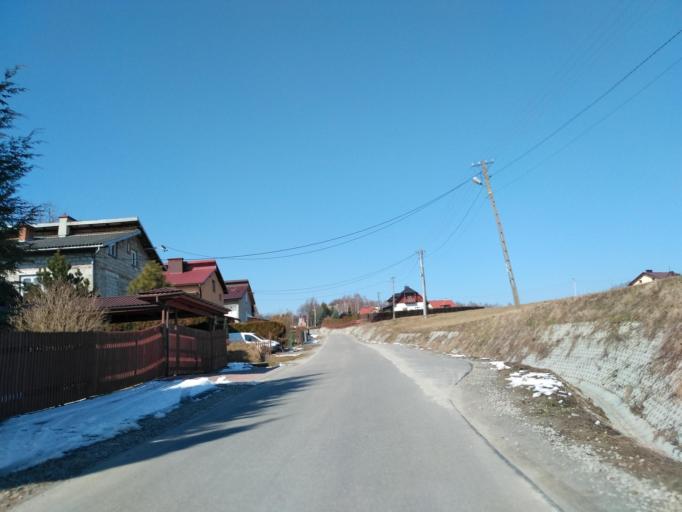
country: PL
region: Subcarpathian Voivodeship
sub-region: Powiat brzozowski
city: Jasienica Rosielna
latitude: 49.7542
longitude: 21.9415
